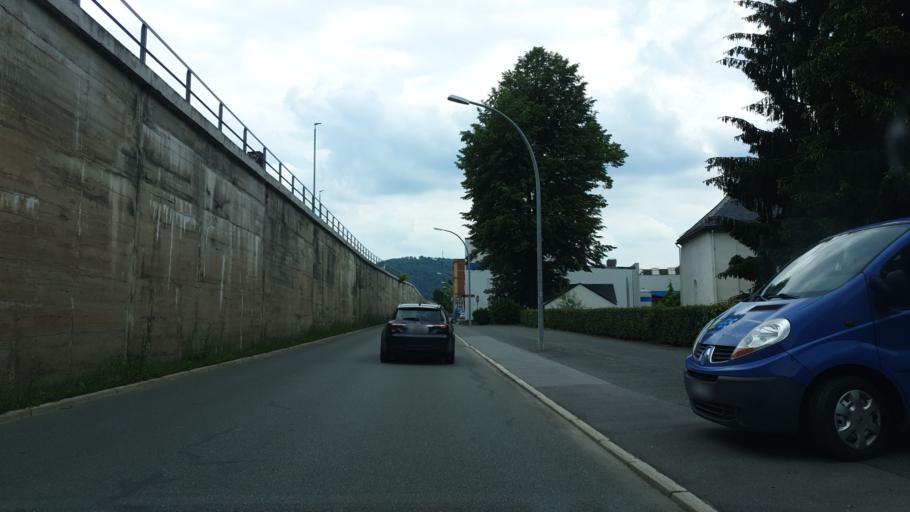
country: DE
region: Saxony
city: Aue
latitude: 50.5986
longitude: 12.6932
